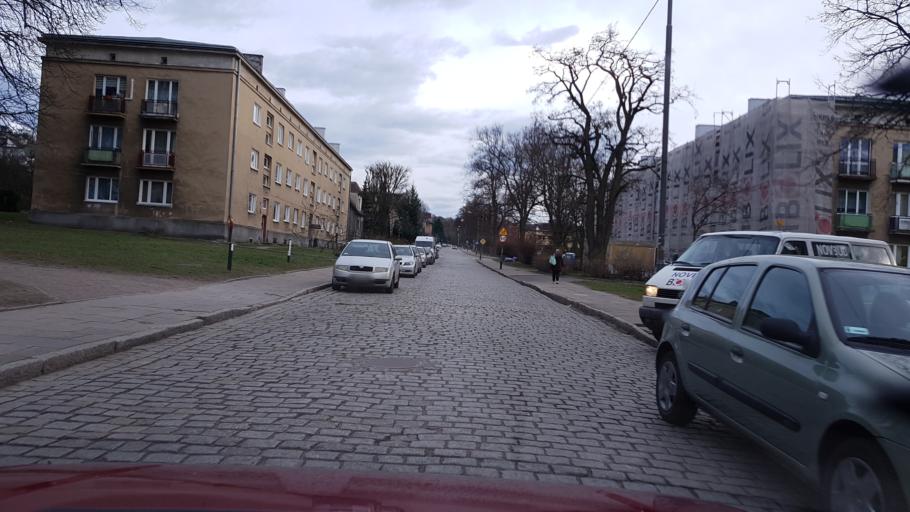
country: PL
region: West Pomeranian Voivodeship
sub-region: Szczecin
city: Szczecin
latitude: 53.3658
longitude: 14.5986
